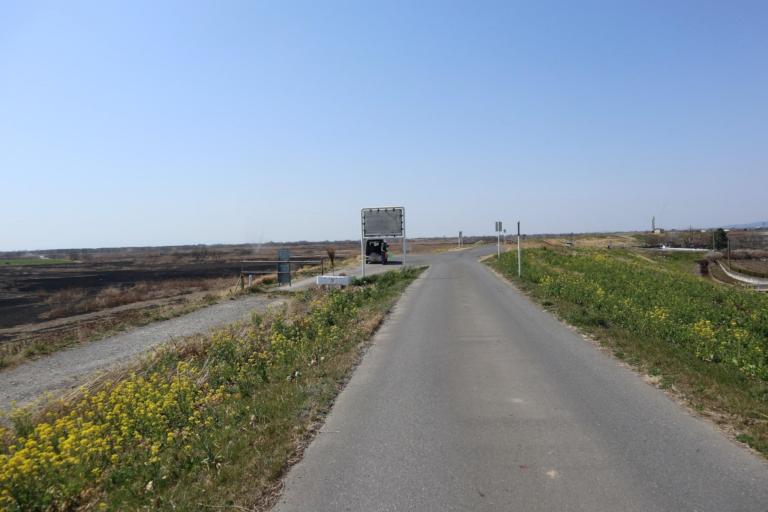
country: JP
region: Ibaraki
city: Koga
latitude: 36.2398
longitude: 139.7095
